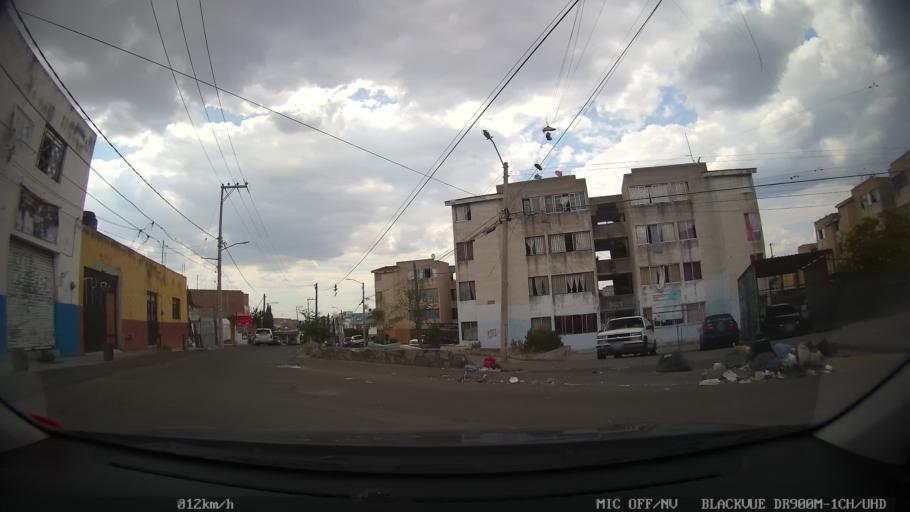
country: MX
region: Jalisco
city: Tlaquepaque
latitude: 20.6320
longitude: -103.2759
